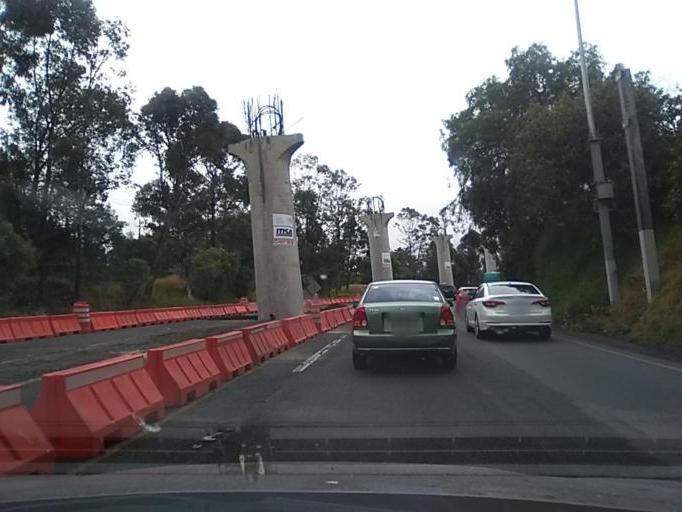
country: MX
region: Mexico City
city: Xochimilco
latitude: 19.2456
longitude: -99.1511
